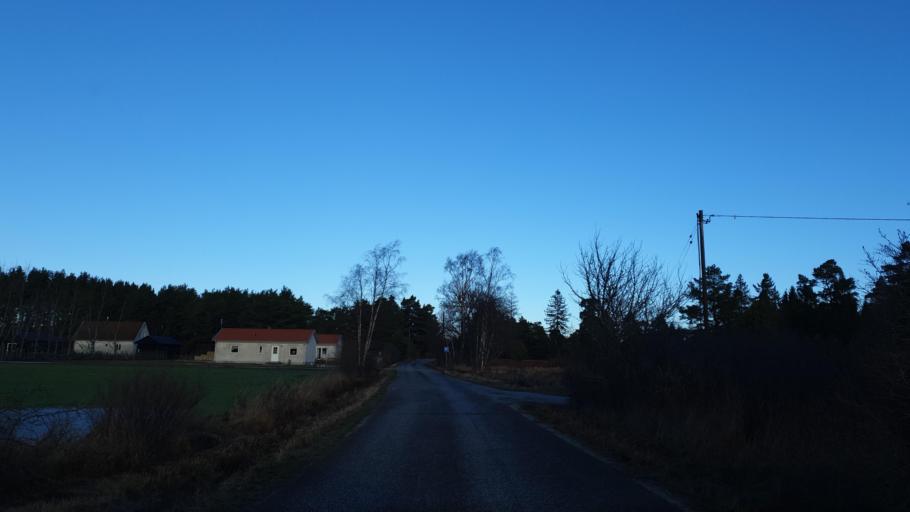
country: SE
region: Gotland
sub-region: Gotland
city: Slite
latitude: 57.3844
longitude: 18.8086
